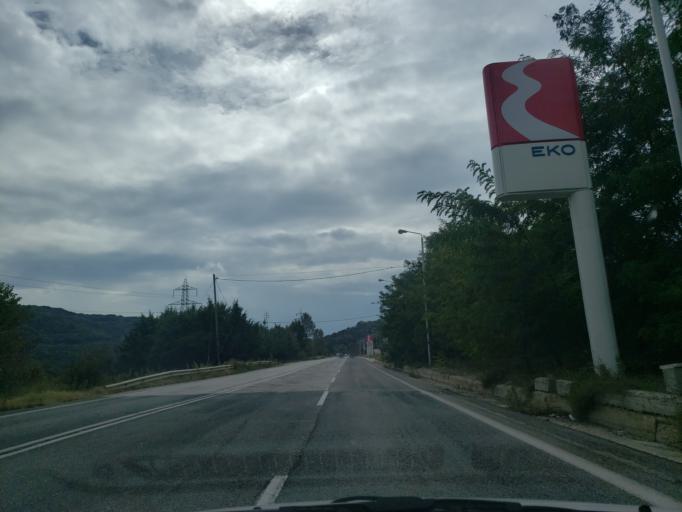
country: GR
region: Central Greece
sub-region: Nomos Fthiotidos
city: Stavros
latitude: 38.9979
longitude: 22.3715
